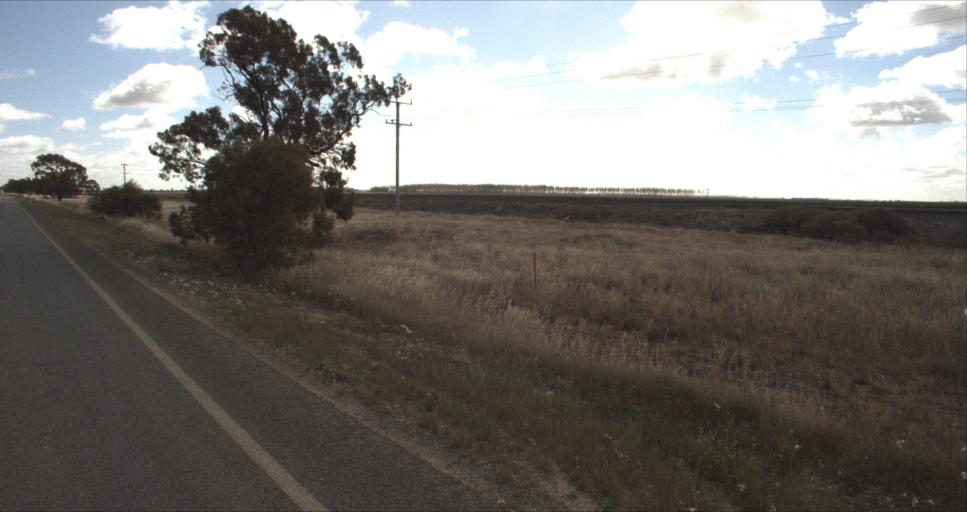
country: AU
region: New South Wales
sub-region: Murrumbidgee Shire
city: Darlington Point
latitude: -34.5701
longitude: 146.1673
